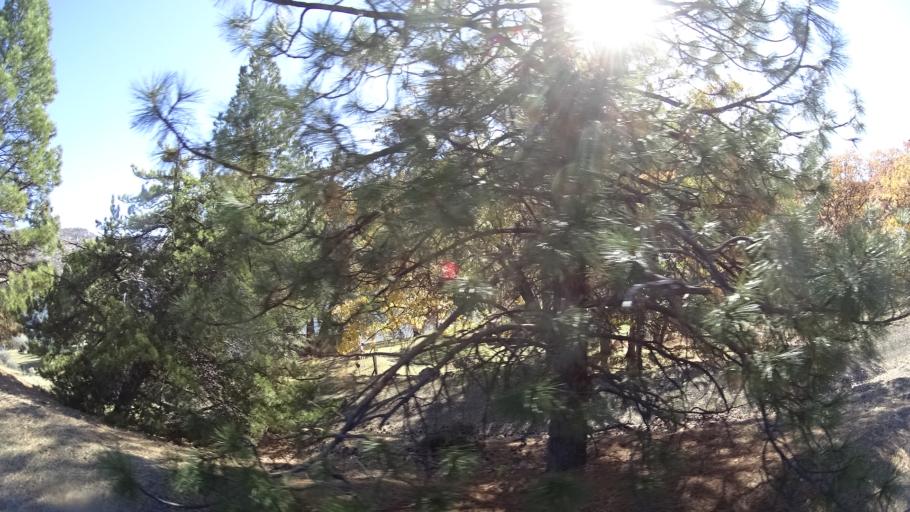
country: US
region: California
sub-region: Siskiyou County
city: Montague
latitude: 41.9751
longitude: -122.3017
